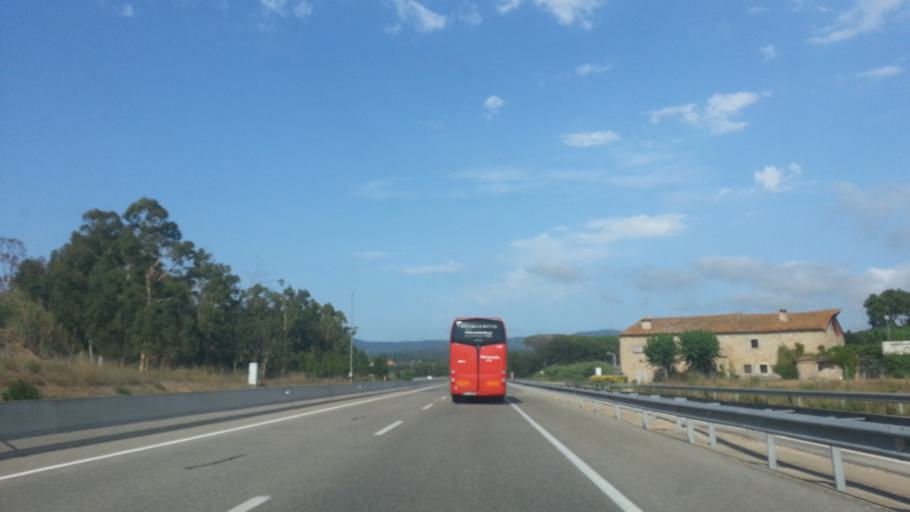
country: ES
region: Catalonia
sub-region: Provincia de Girona
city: Llagostera
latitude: 41.8242
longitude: 2.9147
